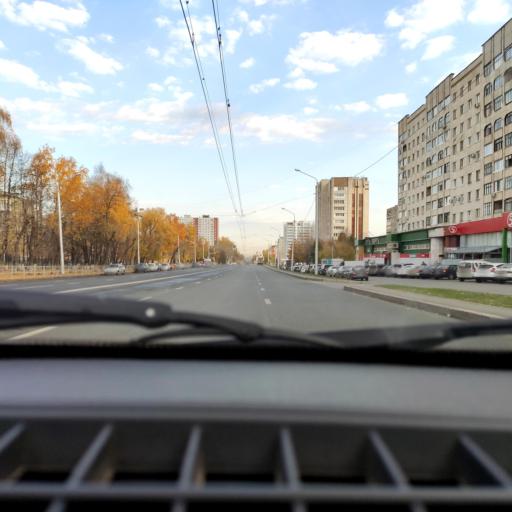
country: RU
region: Bashkortostan
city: Ufa
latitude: 54.7785
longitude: 56.0361
